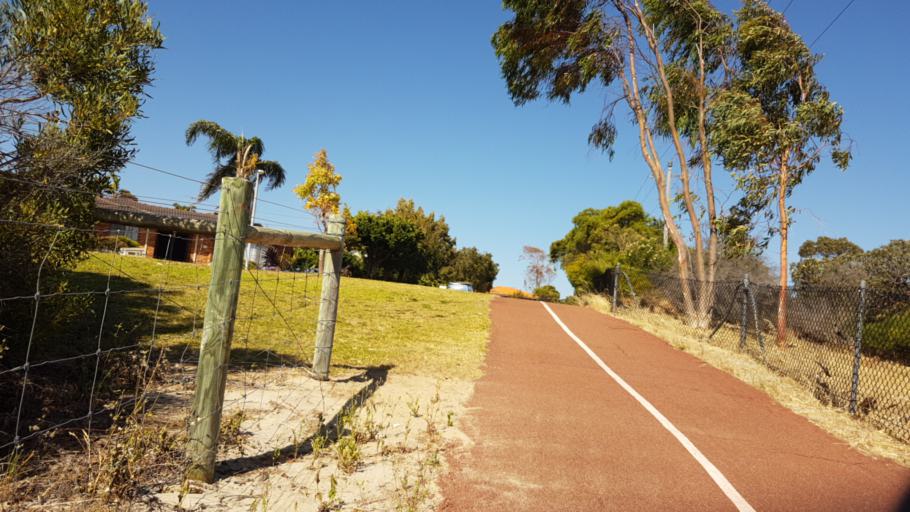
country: AU
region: Western Australia
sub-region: Stirling
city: North Beach
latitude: -31.8573
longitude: 115.7706
